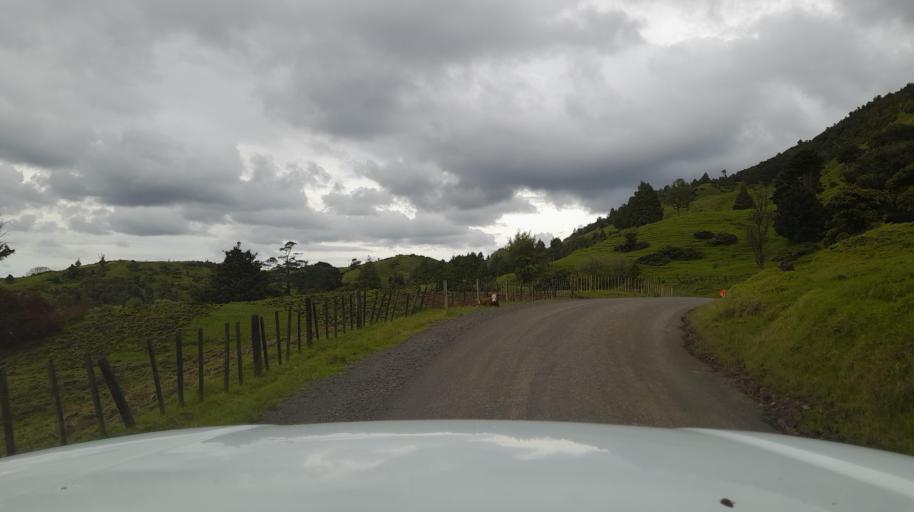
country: NZ
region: Northland
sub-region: Far North District
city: Kaitaia
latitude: -35.3402
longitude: 173.3592
